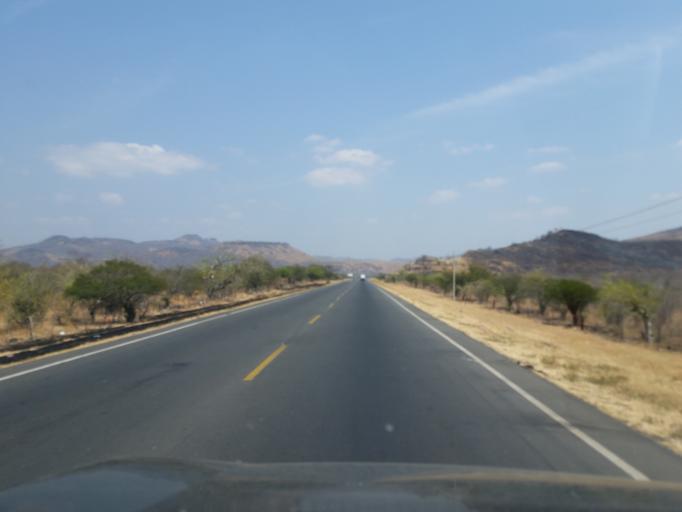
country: NI
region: Managua
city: Tipitapa
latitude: 12.4185
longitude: -86.0412
